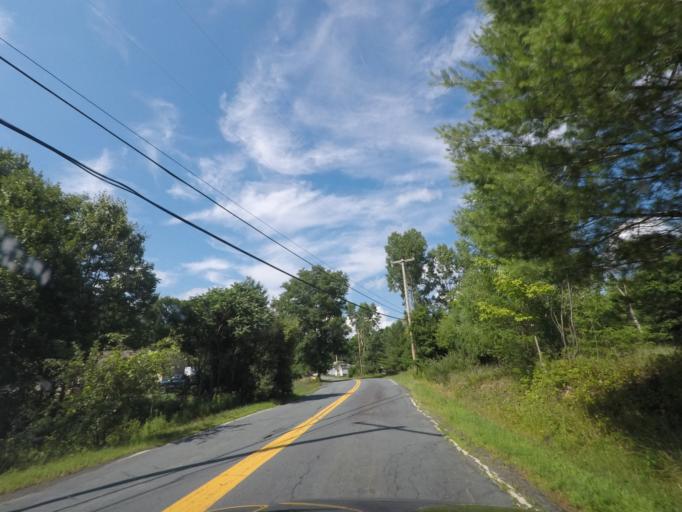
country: US
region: New York
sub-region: Rensselaer County
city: Averill Park
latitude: 42.5835
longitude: -73.5702
